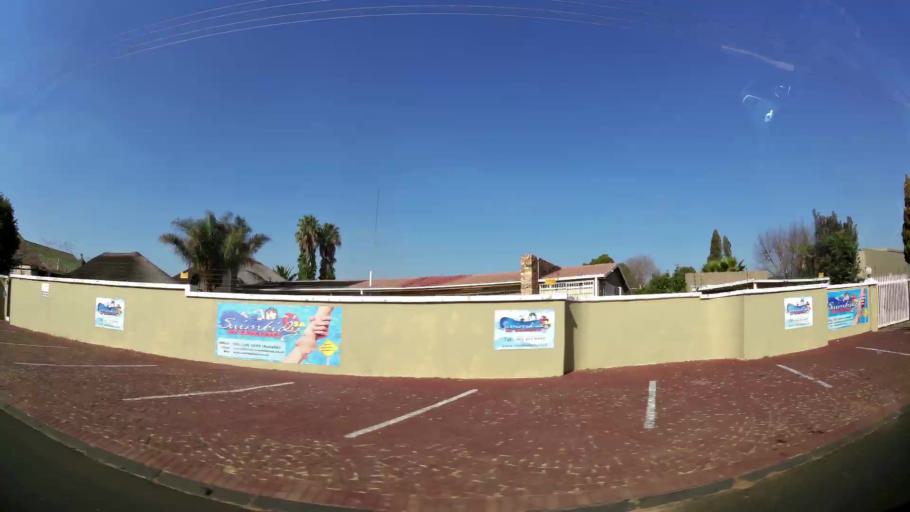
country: ZA
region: Gauteng
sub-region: West Rand District Municipality
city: Randfontein
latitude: -26.1638
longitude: 27.6900
